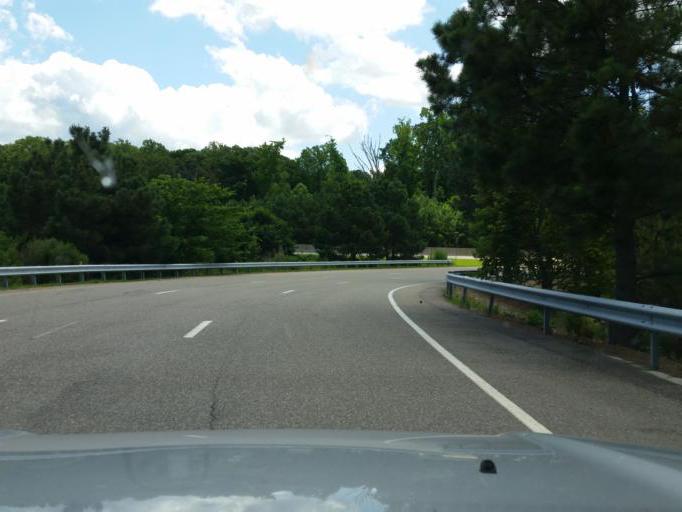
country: US
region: Virginia
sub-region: City of Williamsburg
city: Williamsburg
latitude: 37.2356
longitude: -76.6370
